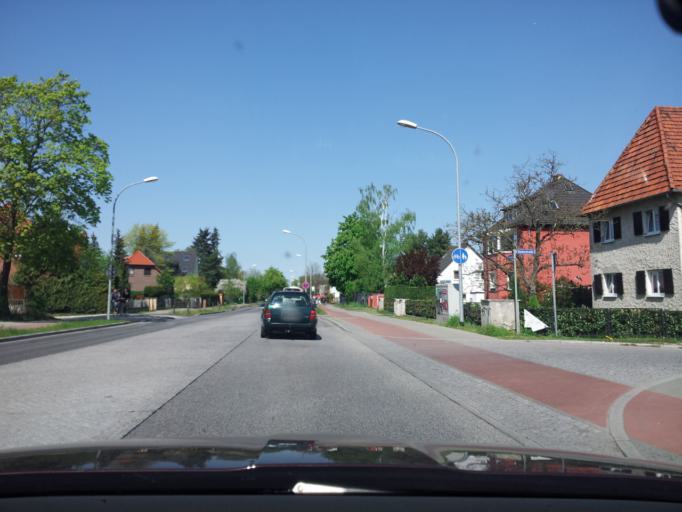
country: DE
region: Brandenburg
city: Teltow
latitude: 52.3917
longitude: 13.2920
